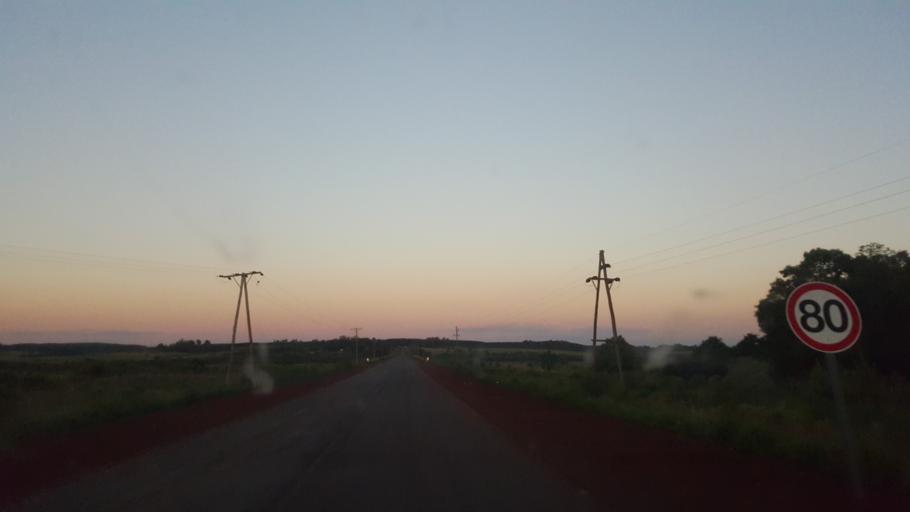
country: AR
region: Corrientes
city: Garruchos
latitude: -28.2368
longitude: -55.8210
